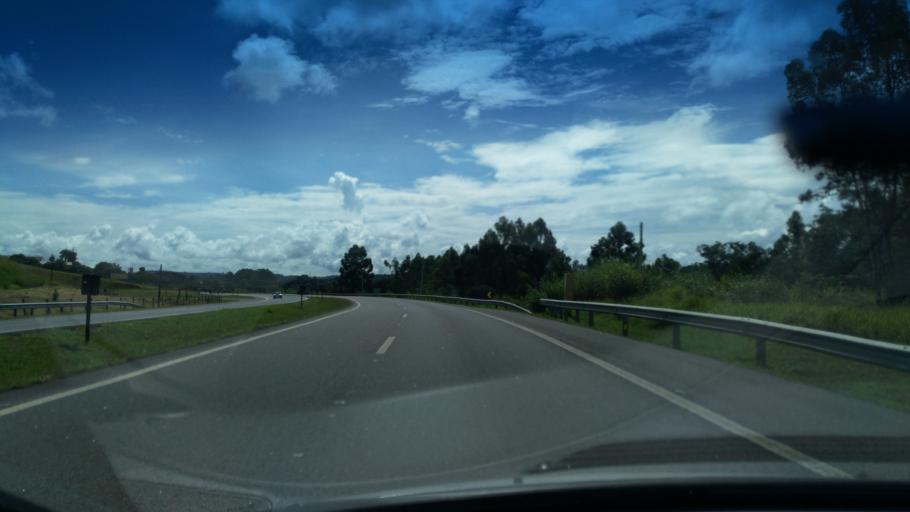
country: BR
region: Sao Paulo
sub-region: Santo Antonio Do Jardim
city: Espirito Santo do Pinhal
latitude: -22.2067
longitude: -46.7785
